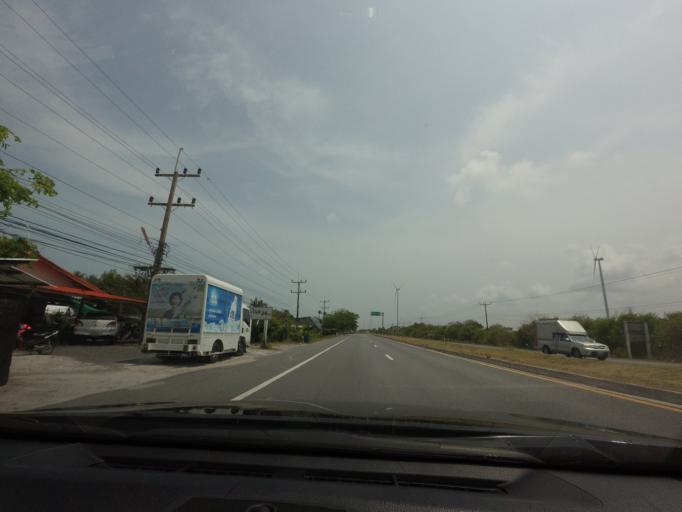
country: TH
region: Nakhon Si Thammarat
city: Hua Sai
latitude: 7.9760
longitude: 100.3268
